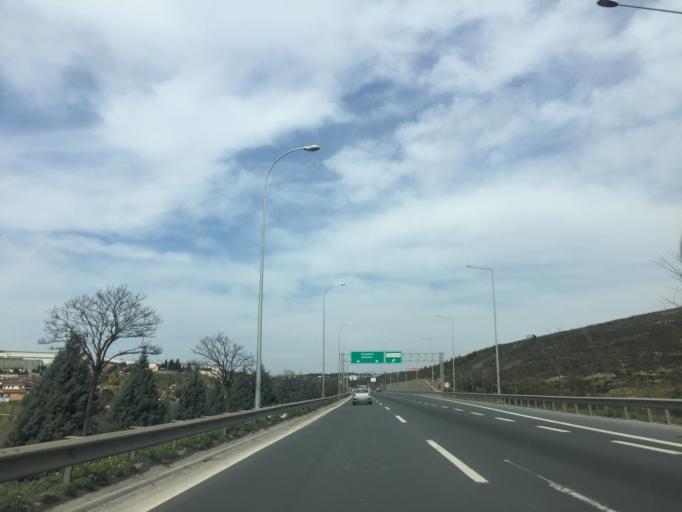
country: TR
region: Kocaeli
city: Darica
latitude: 40.8362
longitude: 29.3717
